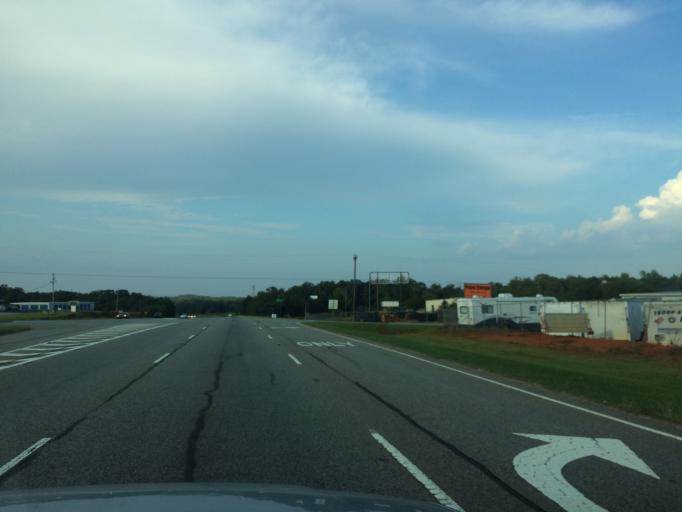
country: US
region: South Carolina
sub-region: Anderson County
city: Piedmont
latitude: 34.6755
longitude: -82.5099
